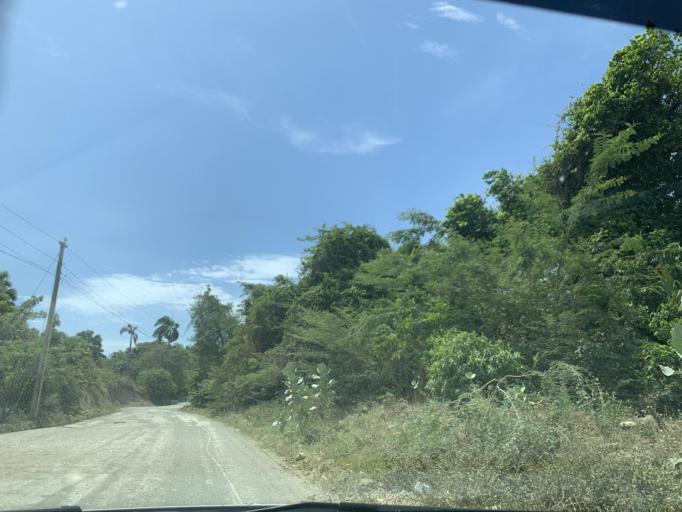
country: DO
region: Puerto Plata
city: Imbert
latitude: 19.8647
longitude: -70.8113
